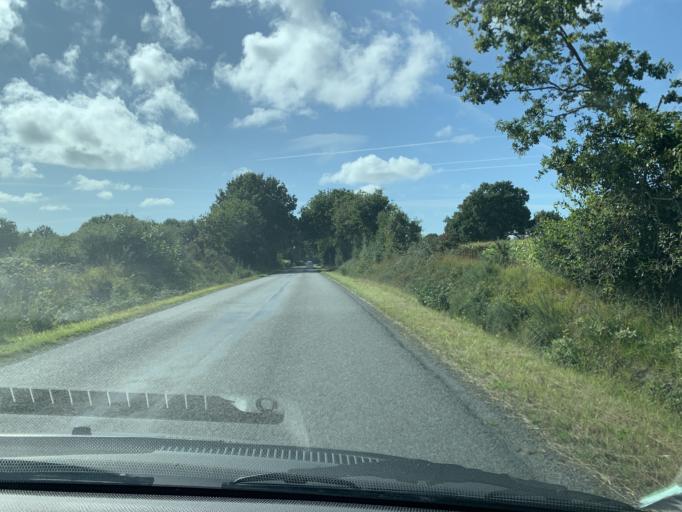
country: FR
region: Pays de la Loire
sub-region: Departement de la Loire-Atlantique
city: Asserac
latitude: 47.4237
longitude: -2.3787
